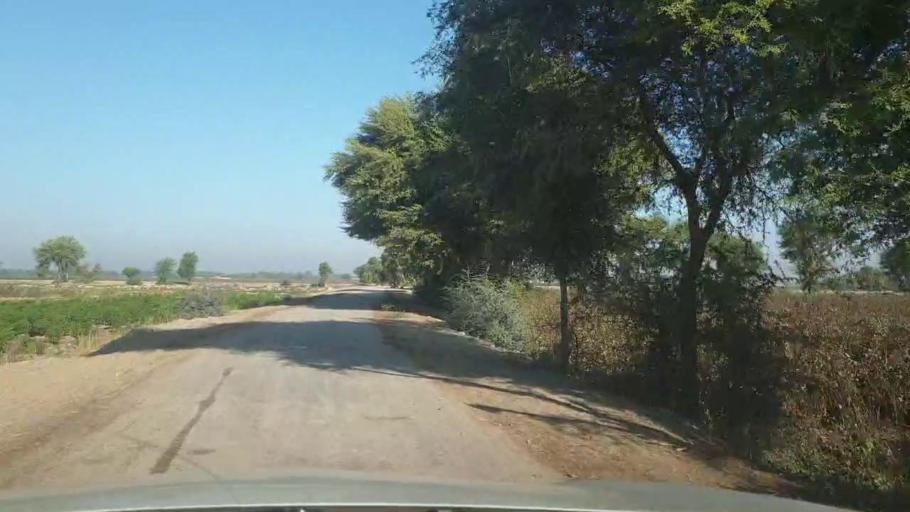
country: PK
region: Sindh
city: Bhan
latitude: 26.5393
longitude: 67.6895
